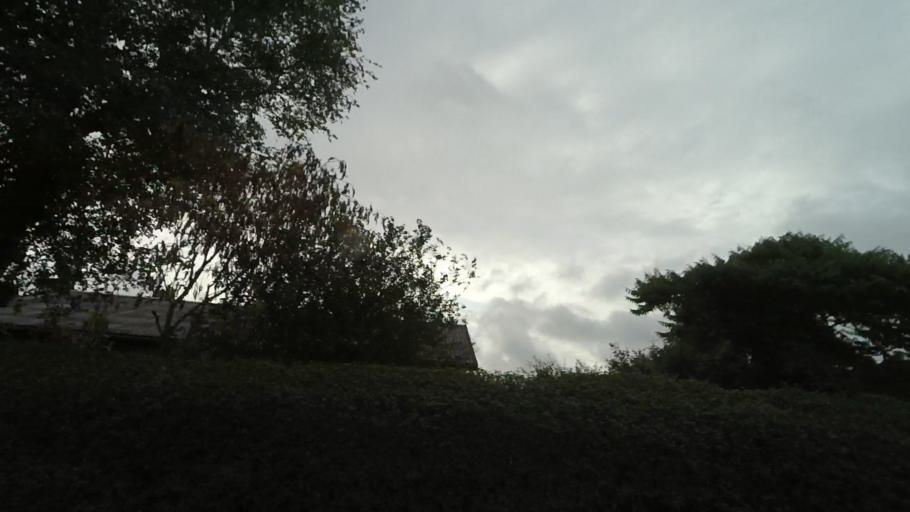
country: DK
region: Central Jutland
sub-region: Syddjurs Kommune
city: Ronde
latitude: 56.3393
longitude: 10.4596
